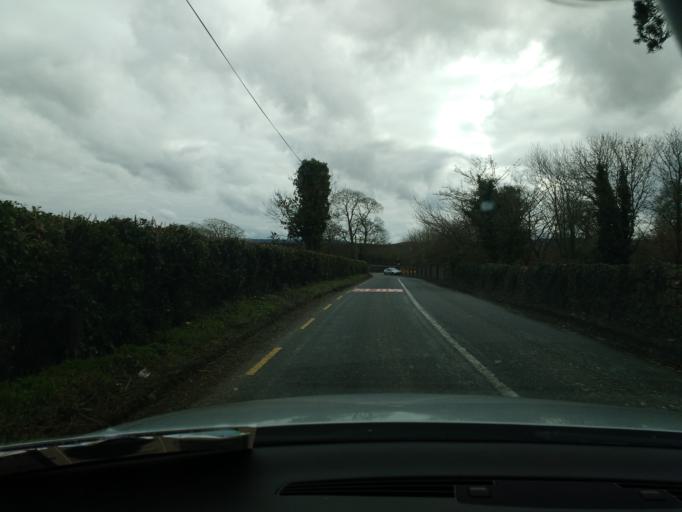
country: IE
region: Leinster
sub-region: Laois
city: Rathdowney
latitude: 52.7224
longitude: -7.5603
